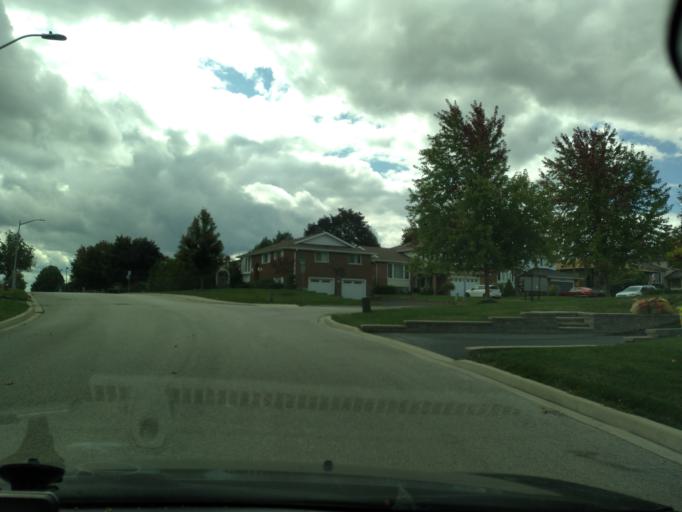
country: CA
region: Ontario
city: Bradford West Gwillimbury
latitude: 44.1246
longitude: -79.5639
